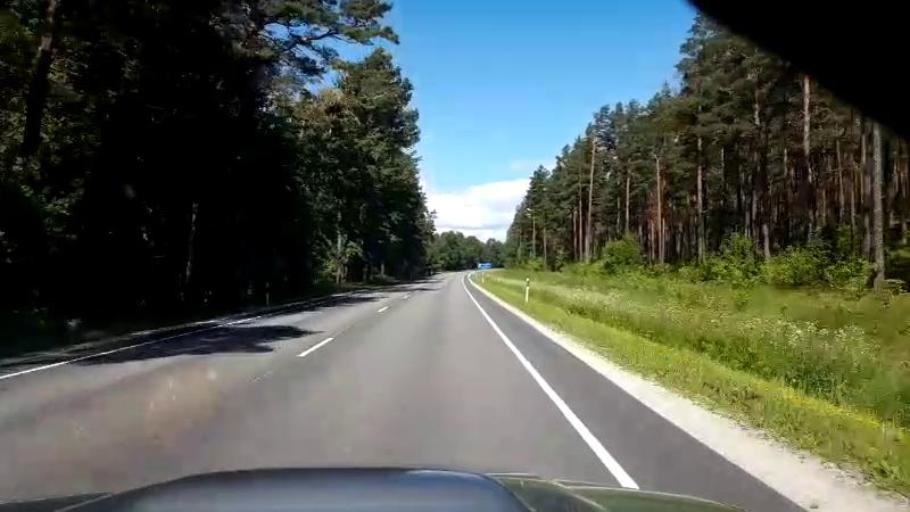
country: EE
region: Paernumaa
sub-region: Paernu linn
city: Parnu
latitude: 58.1532
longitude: 24.4987
